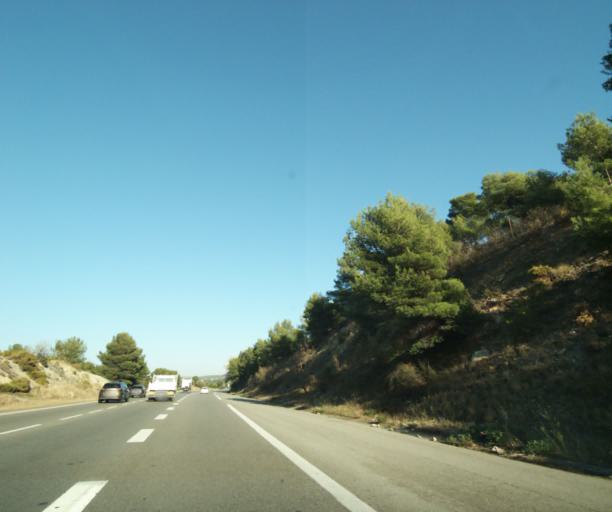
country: FR
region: Provence-Alpes-Cote d'Azur
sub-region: Departement des Bouches-du-Rhone
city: Les Pennes-Mirabeau
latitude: 43.3962
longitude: 5.2853
